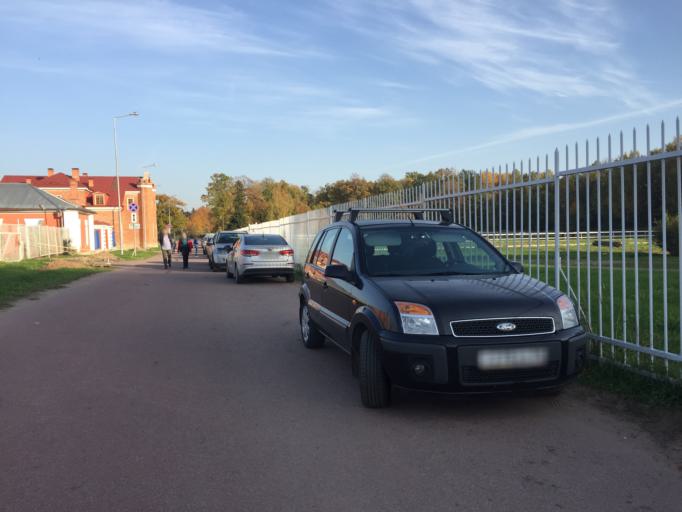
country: RU
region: St.-Petersburg
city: Pushkin
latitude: 59.7251
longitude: 30.3816
